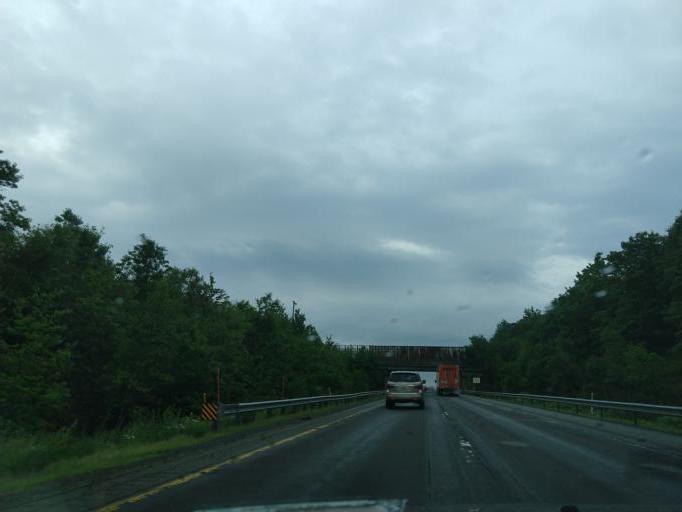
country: US
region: Pennsylvania
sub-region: Schuylkill County
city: McAdoo
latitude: 40.9101
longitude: -76.0224
